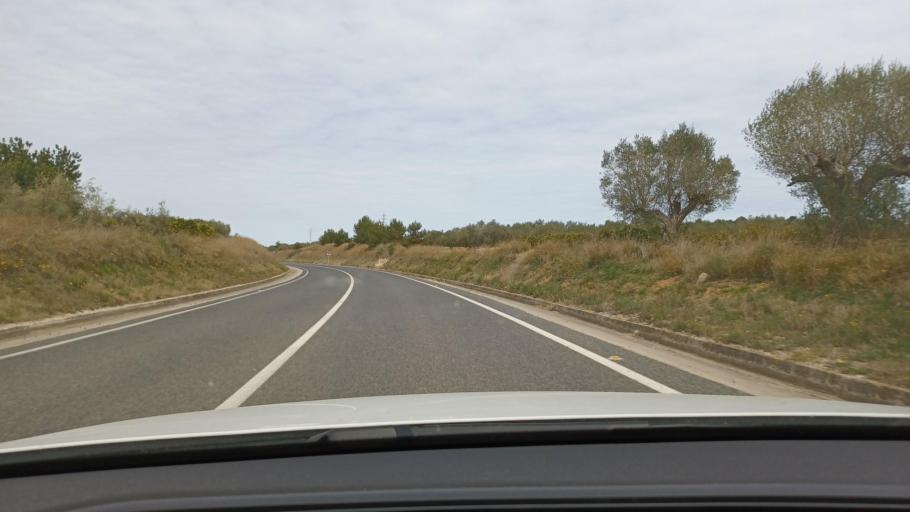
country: ES
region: Catalonia
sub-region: Provincia de Tarragona
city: Masdenverge
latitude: 40.6735
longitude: 0.5260
